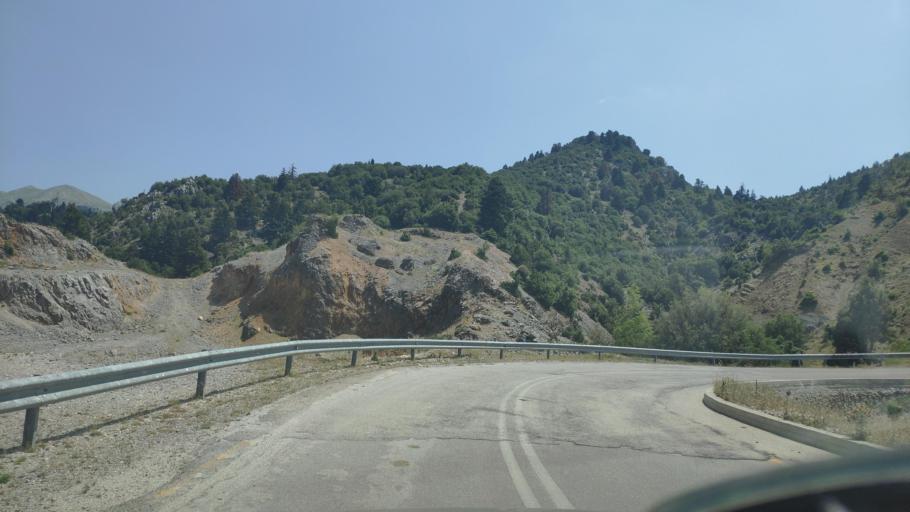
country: GR
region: Epirus
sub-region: Nomos Artas
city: Ano Kalentini
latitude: 39.2506
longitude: 21.2411
